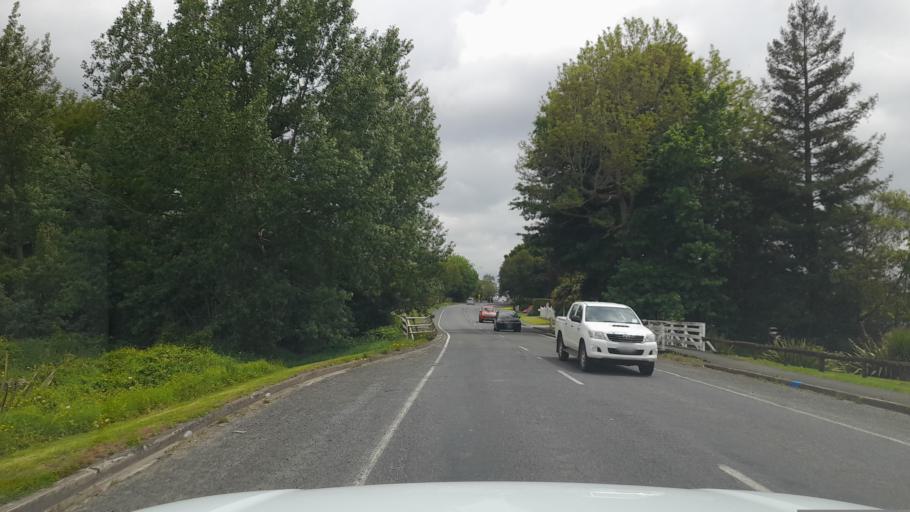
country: NZ
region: Northland
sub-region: Far North District
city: Waimate North
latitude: -35.4035
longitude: 173.8076
